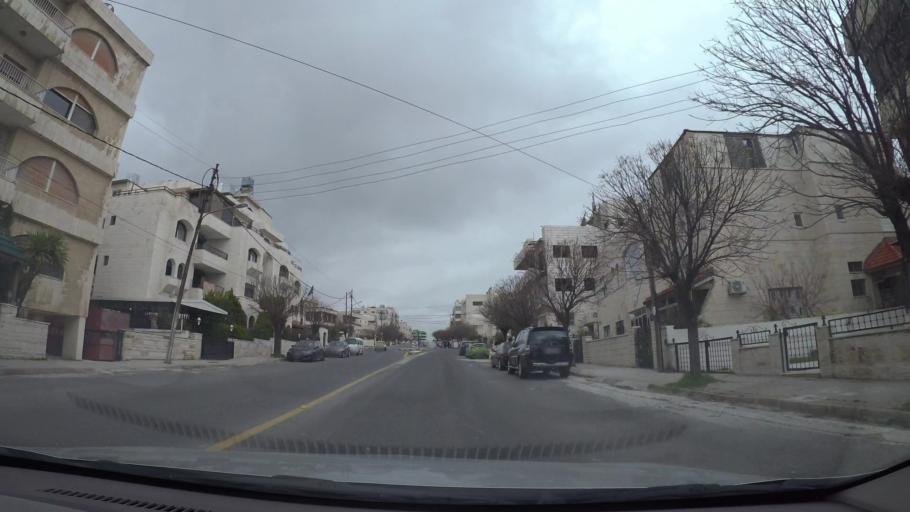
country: JO
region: Amman
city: Wadi as Sir
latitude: 31.9723
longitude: 35.8520
